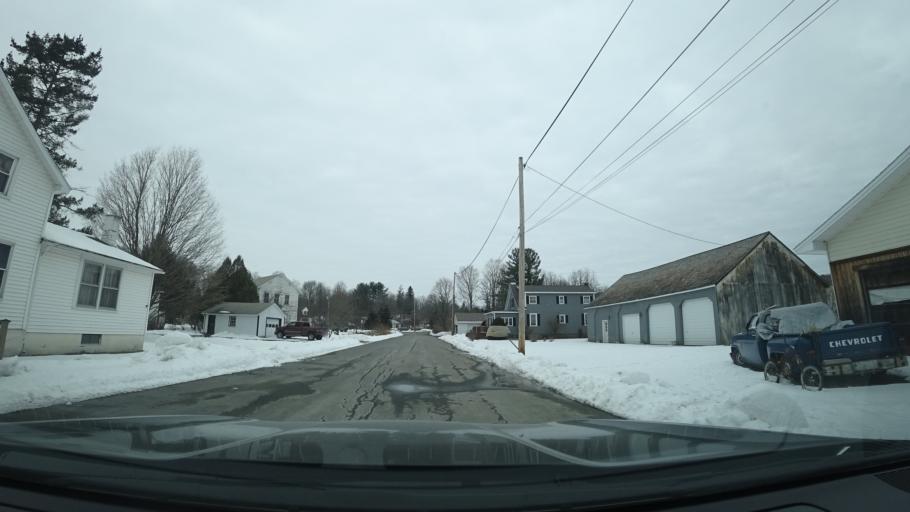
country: US
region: New York
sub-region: Washington County
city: Cambridge
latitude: 43.1769
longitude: -73.3269
